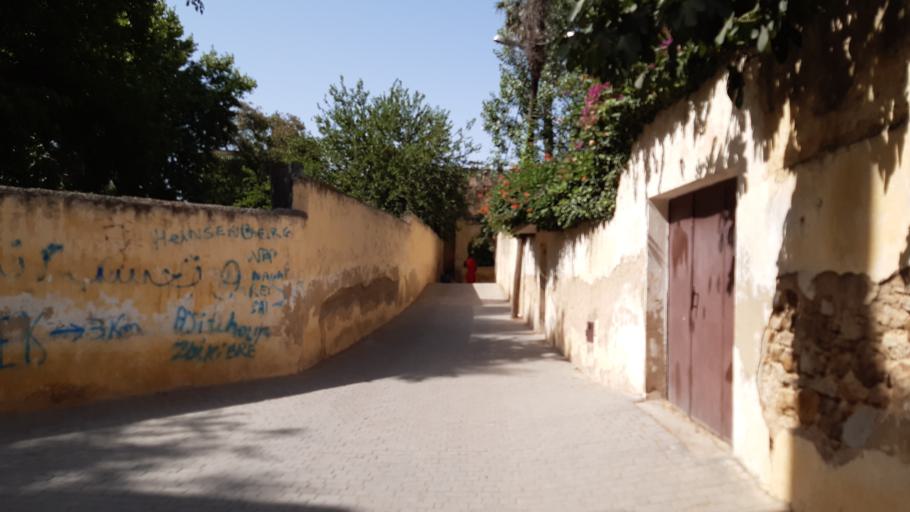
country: MA
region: Fes-Boulemane
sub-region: Fes
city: Fes
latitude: 34.0586
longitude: -4.9898
